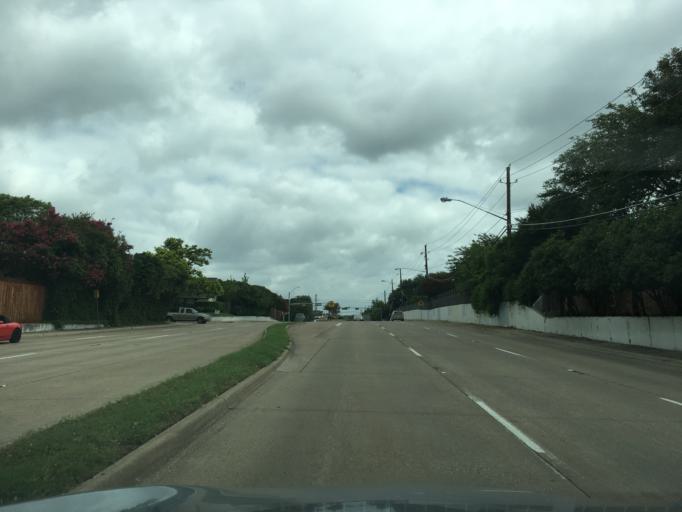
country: US
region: Texas
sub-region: Dallas County
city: Richardson
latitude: 32.8842
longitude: -96.7415
